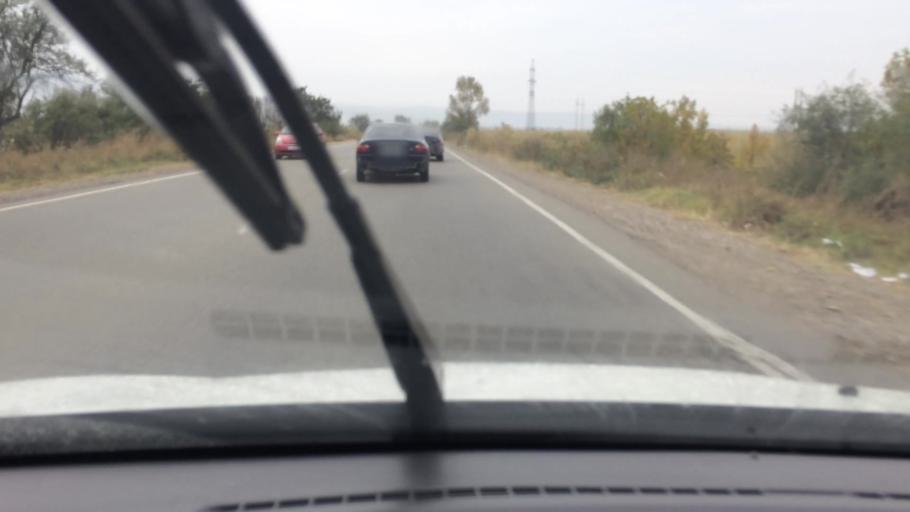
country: GE
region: Kvemo Kartli
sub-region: Marneuli
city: Marneuli
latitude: 41.5379
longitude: 44.7769
